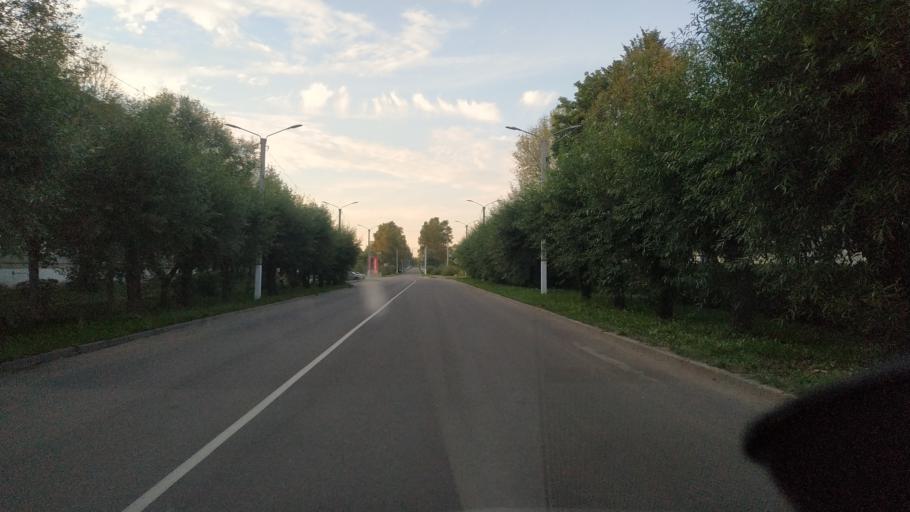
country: RU
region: Moskovskaya
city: Roshal'
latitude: 55.6652
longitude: 39.8526
